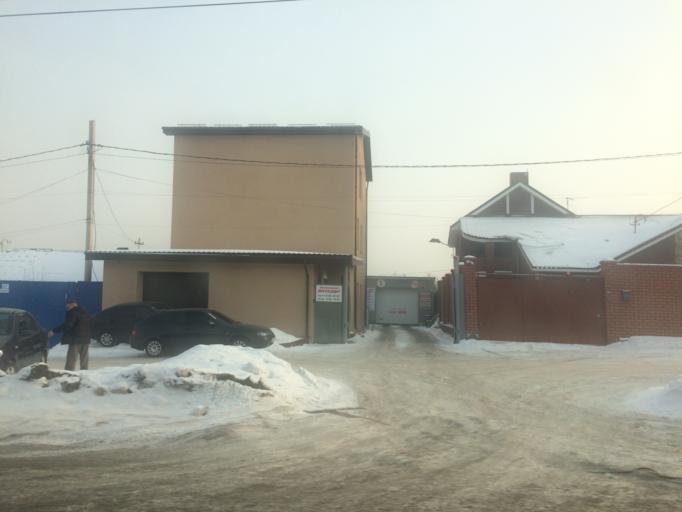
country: RU
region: Chelyabinsk
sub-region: Gorod Magnitogorsk
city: Magnitogorsk
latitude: 53.4308
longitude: 58.9634
